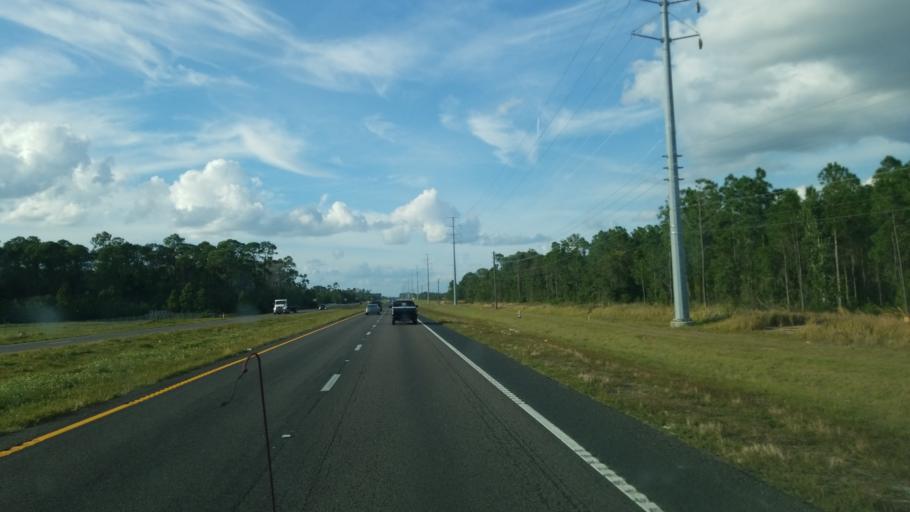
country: US
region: Florida
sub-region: Osceola County
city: Saint Cloud
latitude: 28.2013
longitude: -81.1674
